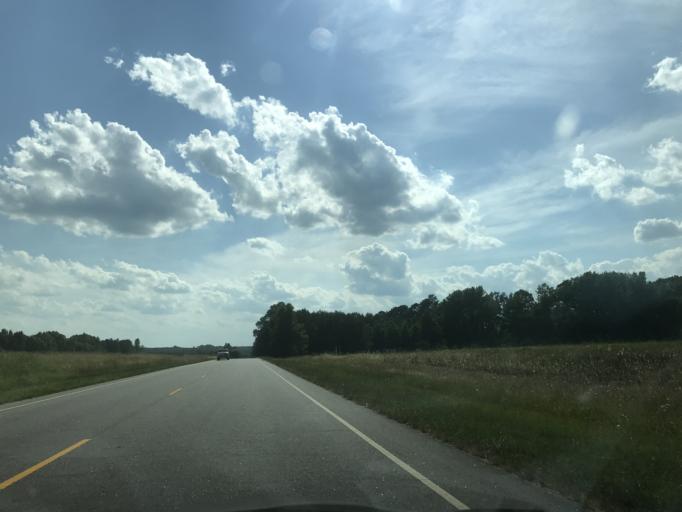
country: US
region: North Carolina
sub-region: Nash County
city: Spring Hope
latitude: 35.9338
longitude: -78.1296
